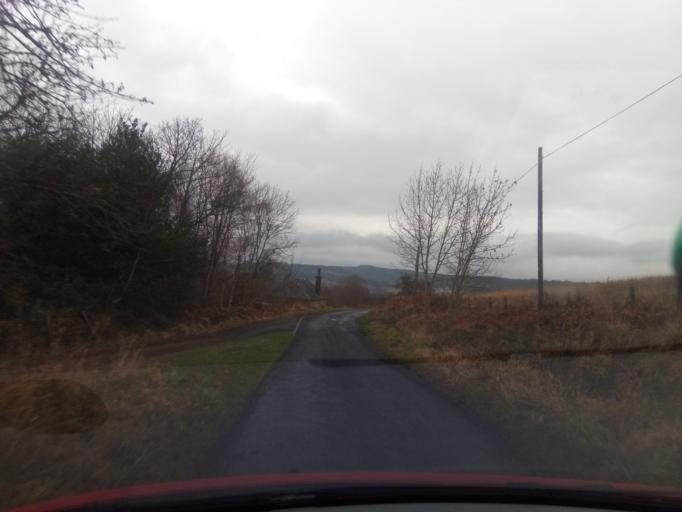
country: GB
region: England
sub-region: Northumberland
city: Rochester
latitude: 55.1761
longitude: -2.4281
